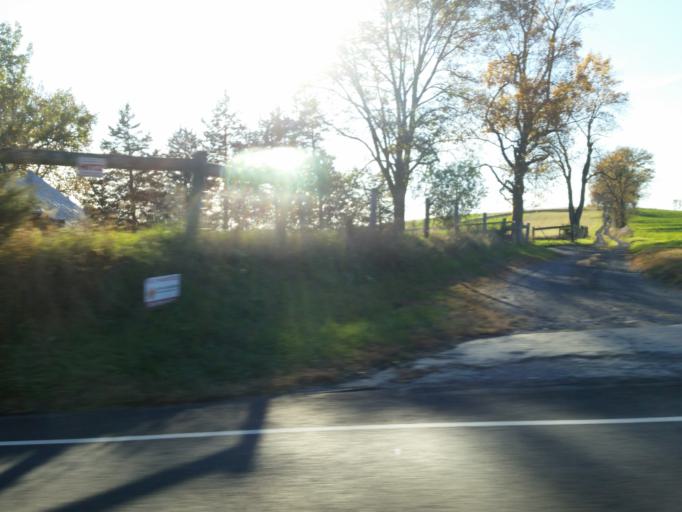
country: US
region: Pennsylvania
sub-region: Lebanon County
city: Annville
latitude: 40.3746
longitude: -76.5518
